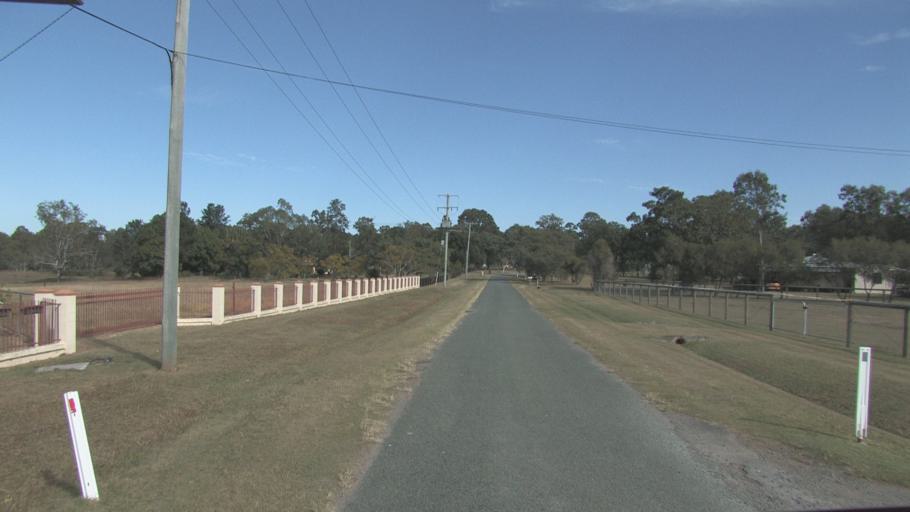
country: AU
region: Queensland
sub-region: Logan
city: North Maclean
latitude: -27.7756
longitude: 152.9965
